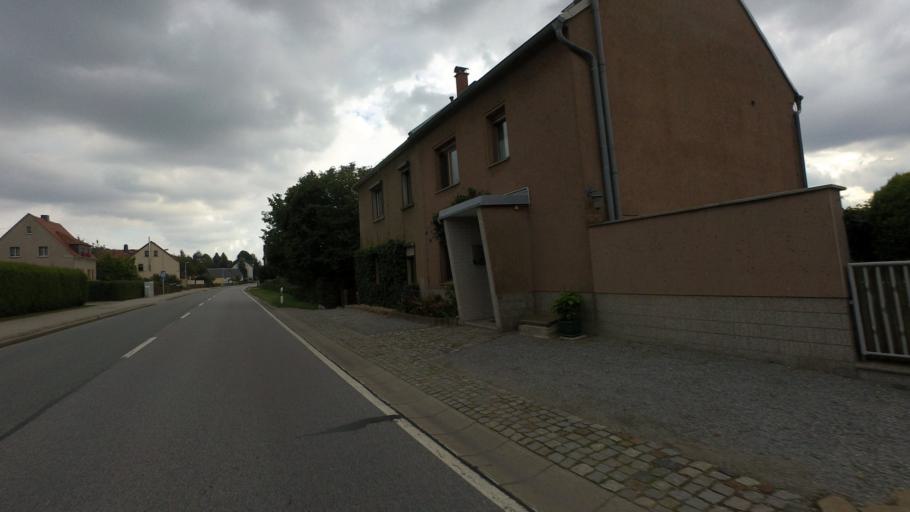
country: DE
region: Saxony
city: Grosspostwitz
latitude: 51.1134
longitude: 14.4532
